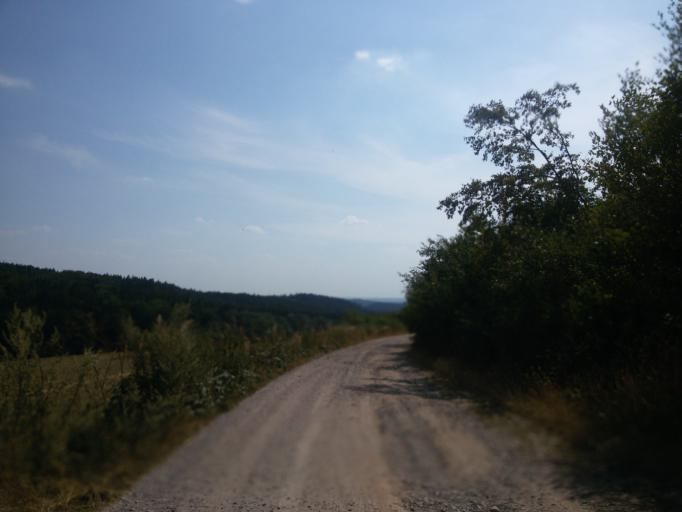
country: CZ
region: South Moravian
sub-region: Okres Brno-Venkov
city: Lomnice
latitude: 49.4393
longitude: 16.4557
